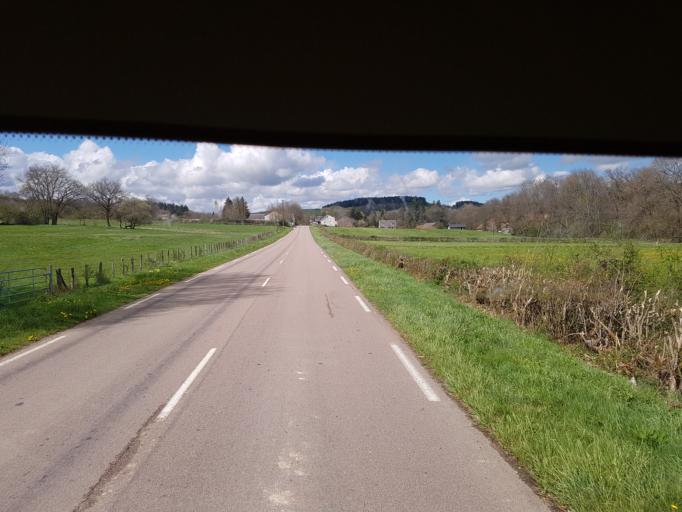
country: FR
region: Bourgogne
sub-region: Departement de la Cote-d'Or
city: Saulieu
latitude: 47.1088
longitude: 4.2286
